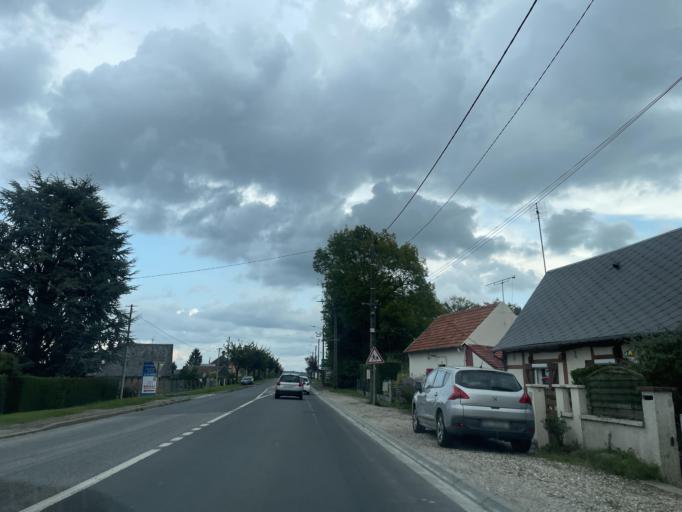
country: FR
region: Haute-Normandie
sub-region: Departement de la Seine-Maritime
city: Gournay-en-Bray
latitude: 49.4860
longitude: 1.6984
